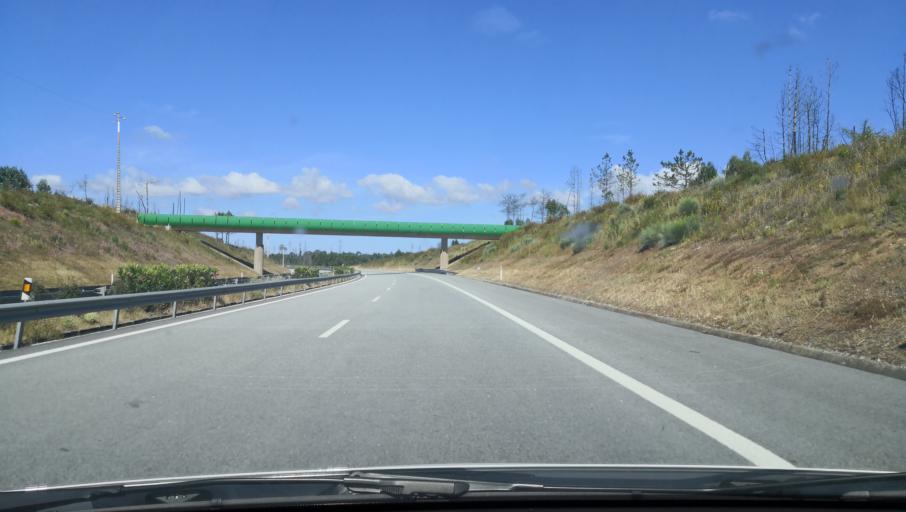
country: PT
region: Coimbra
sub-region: Cantanhede
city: Cantanhede
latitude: 40.2857
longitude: -8.5687
